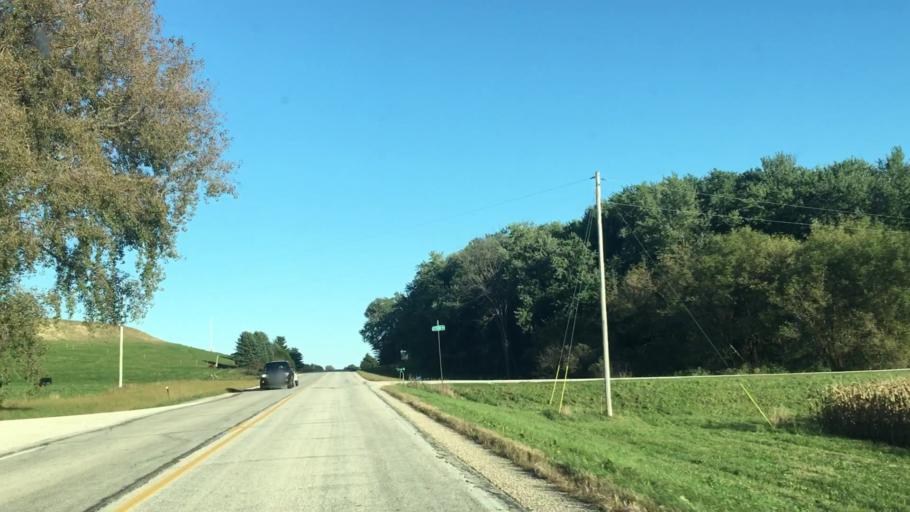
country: US
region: Minnesota
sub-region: Fillmore County
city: Chatfield
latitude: 43.8449
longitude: -92.0998
